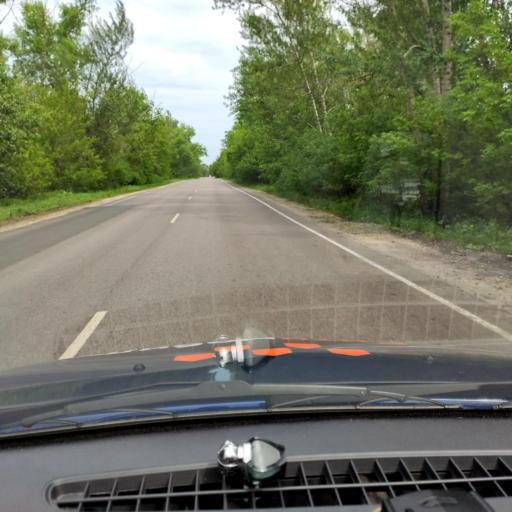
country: RU
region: Voronezj
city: Maslovka
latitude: 51.5302
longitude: 39.3007
